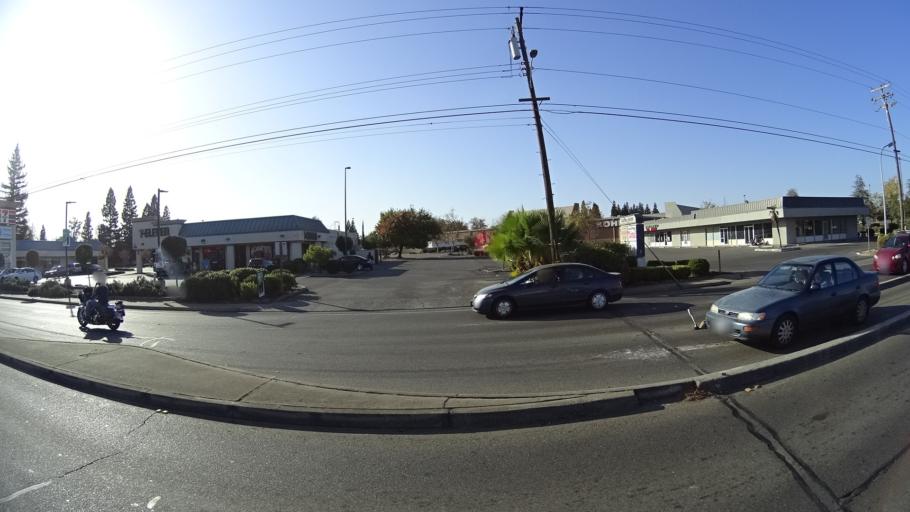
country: US
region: California
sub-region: Sacramento County
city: Citrus Heights
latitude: 38.6759
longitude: -121.2924
